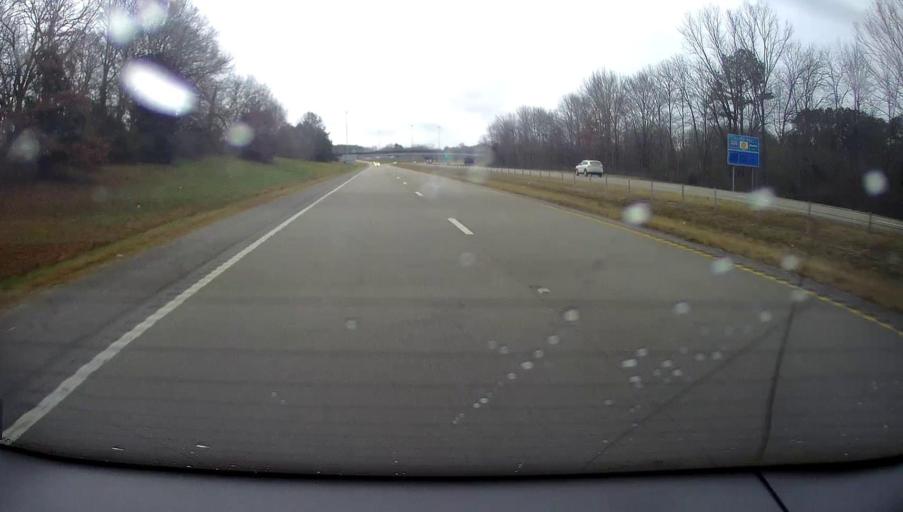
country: US
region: Mississippi
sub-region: Alcorn County
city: Corinth
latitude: 34.9251
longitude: -88.5450
